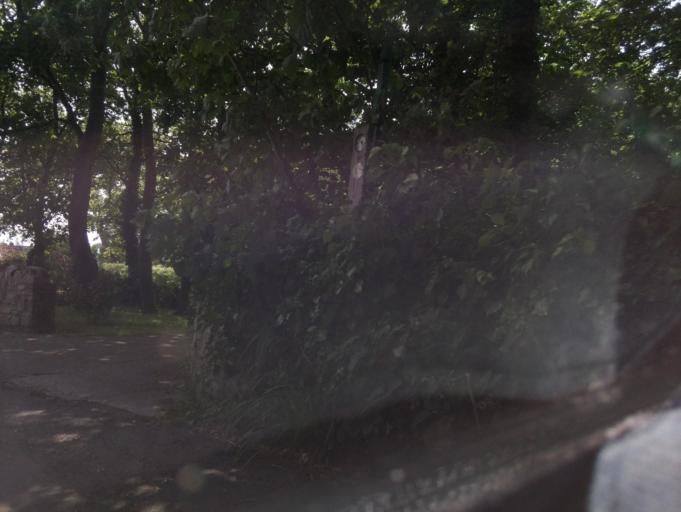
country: GB
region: Wales
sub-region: Vale of Glamorgan
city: Wick
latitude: 51.4068
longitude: -3.5315
